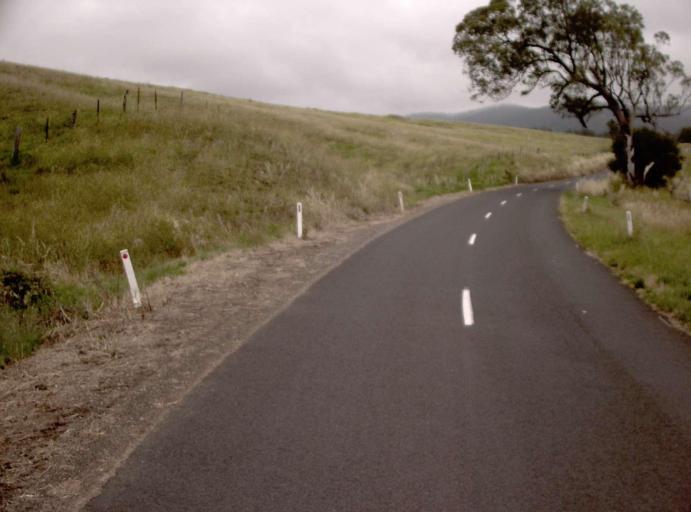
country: AU
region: Victoria
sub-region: Wellington
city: Heyfield
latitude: -37.8450
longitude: 146.6985
